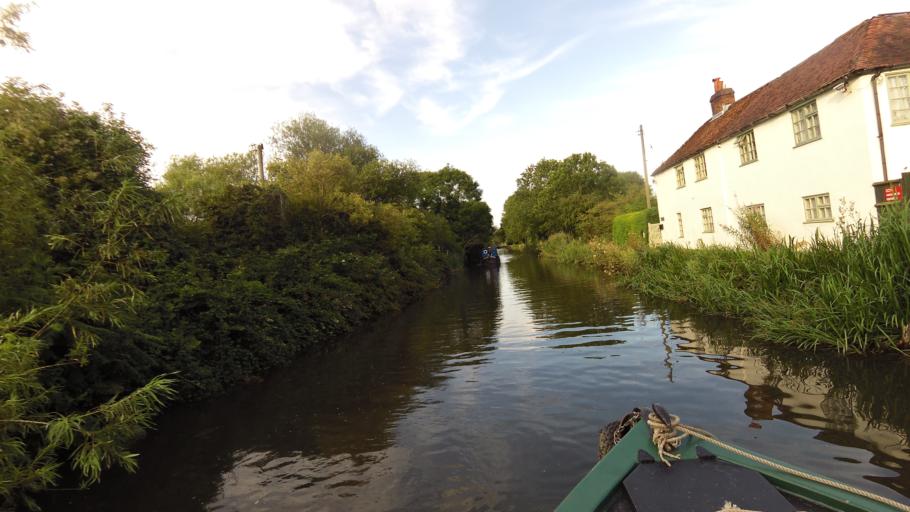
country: GB
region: England
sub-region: West Berkshire
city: Thatcham
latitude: 51.3925
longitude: -1.2001
